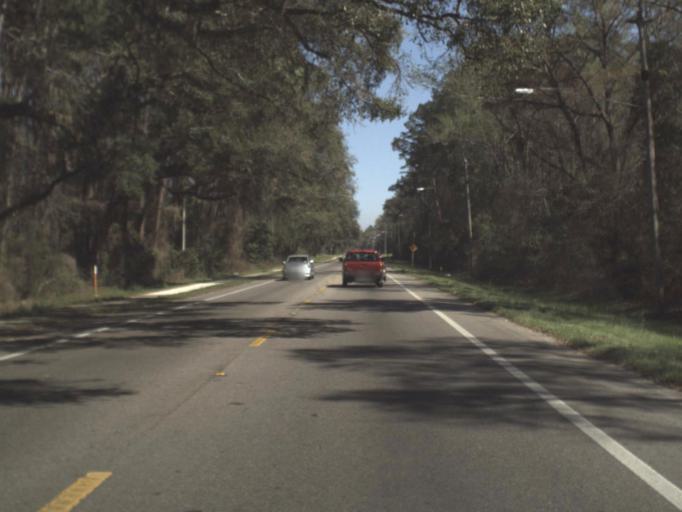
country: US
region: Florida
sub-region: Leon County
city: Tallahassee
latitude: 30.4126
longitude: -84.3207
